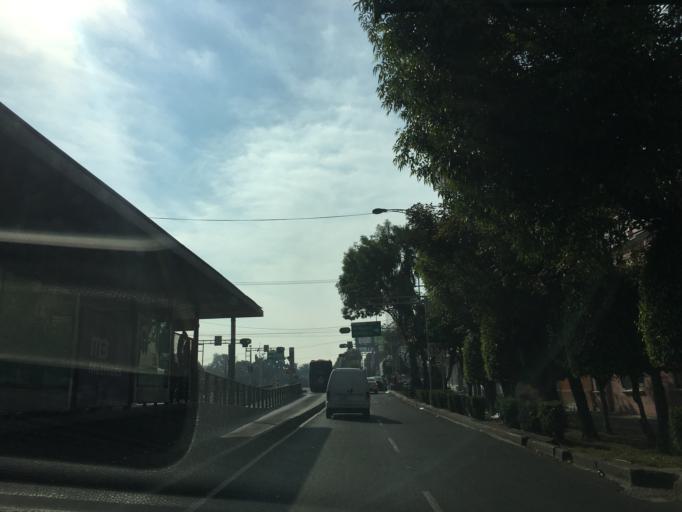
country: MX
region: Mexico City
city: Benito Juarez
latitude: 19.4013
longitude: -99.1681
